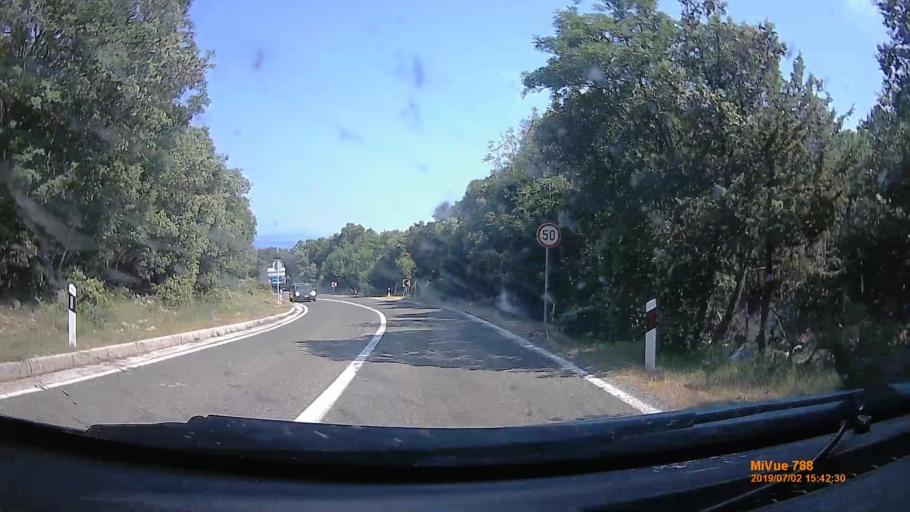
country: HR
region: Primorsko-Goranska
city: Cres
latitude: 44.9555
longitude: 14.4507
